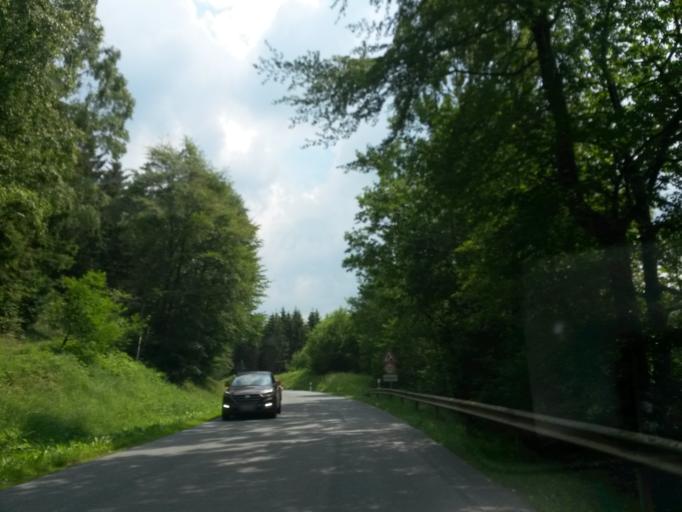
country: DE
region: North Rhine-Westphalia
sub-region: Regierungsbezirk Arnsberg
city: Attendorn
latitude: 51.0649
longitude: 7.9081
